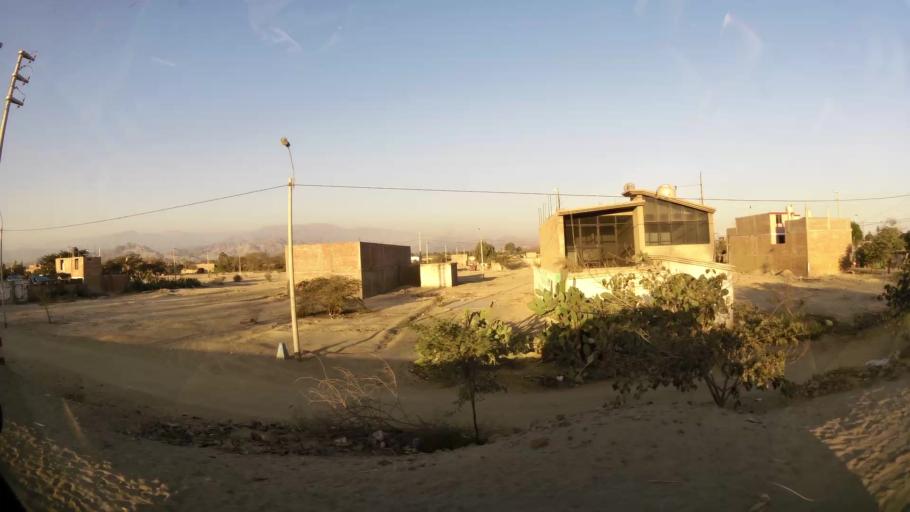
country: PE
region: Ica
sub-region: Provincia de Ica
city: Ica
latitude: -14.0850
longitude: -75.7175
